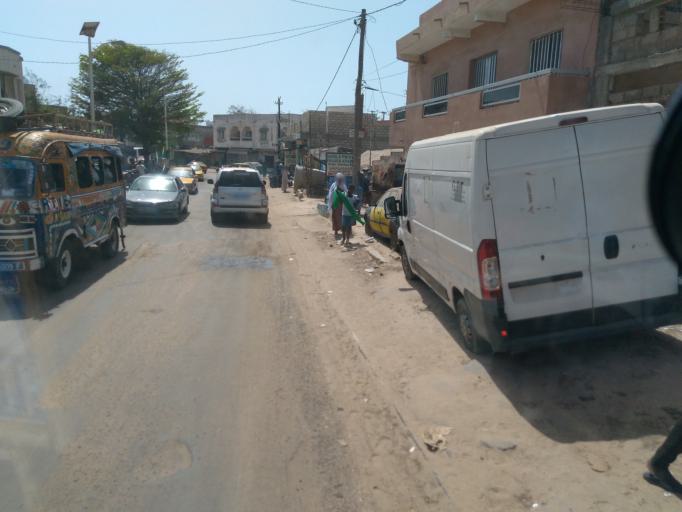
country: SN
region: Dakar
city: Pikine
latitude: 14.7644
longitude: -17.3717
